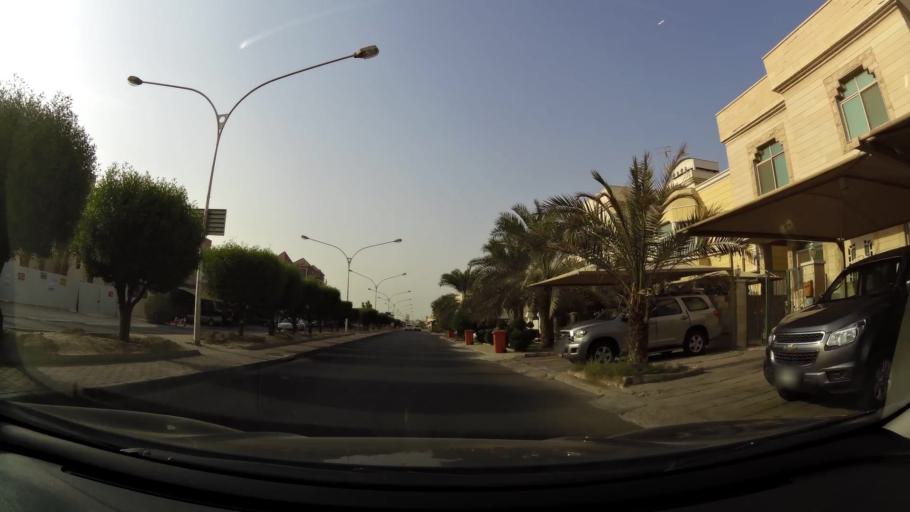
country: KW
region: Muhafazat Hawalli
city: Hawalli
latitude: 29.3105
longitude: 48.0080
